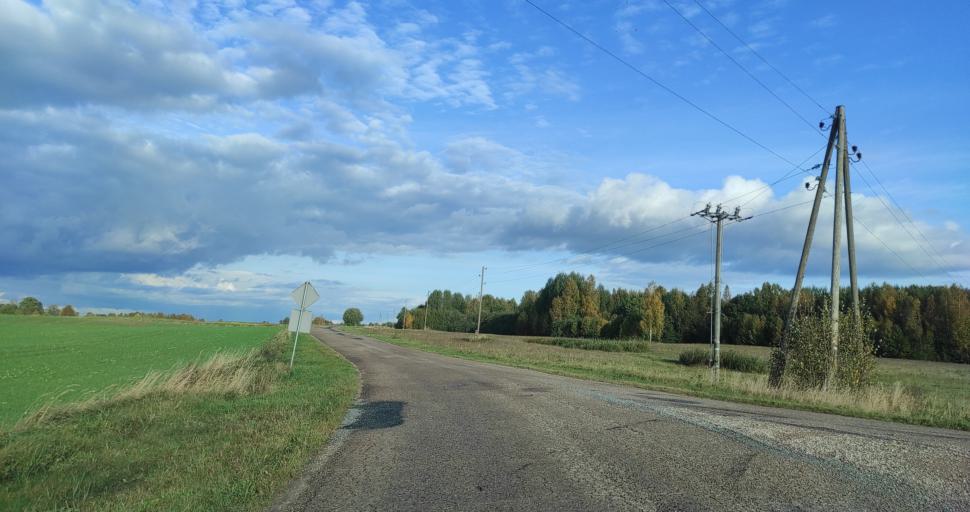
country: LV
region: Aizpute
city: Aizpute
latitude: 56.7729
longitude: 21.7853
